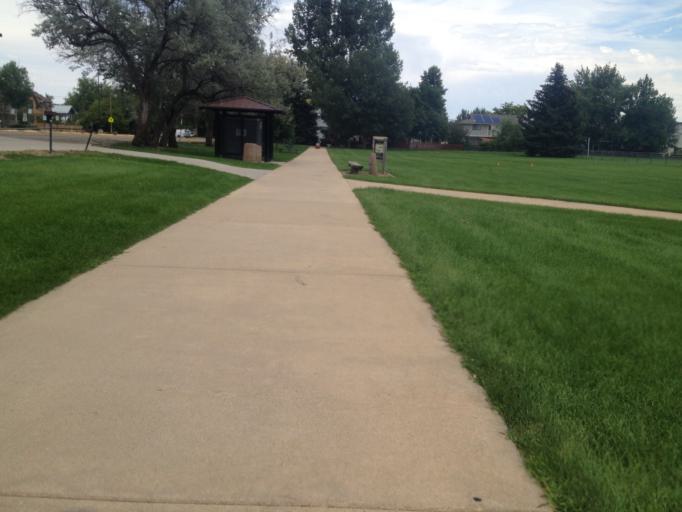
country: US
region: Colorado
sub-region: Boulder County
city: Louisville
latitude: 39.9744
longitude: -105.1388
